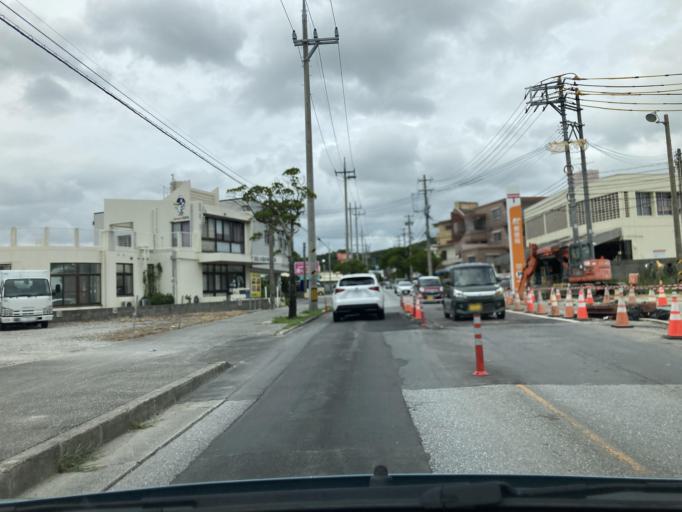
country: JP
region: Okinawa
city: Ginowan
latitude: 26.2261
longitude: 127.7643
